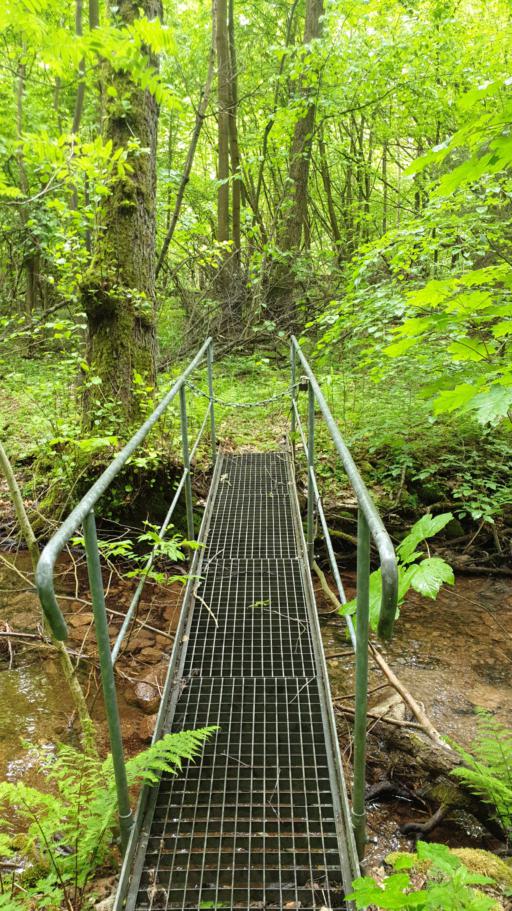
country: DE
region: Saxony
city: Barenstein
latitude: 50.8035
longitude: 13.7738
